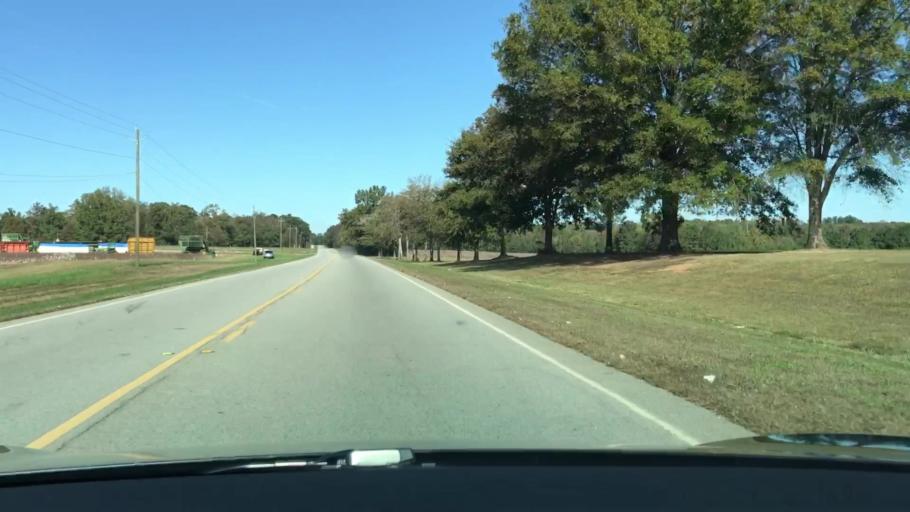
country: US
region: Georgia
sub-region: Warren County
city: West Warrenton
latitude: 33.4247
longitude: -82.6822
